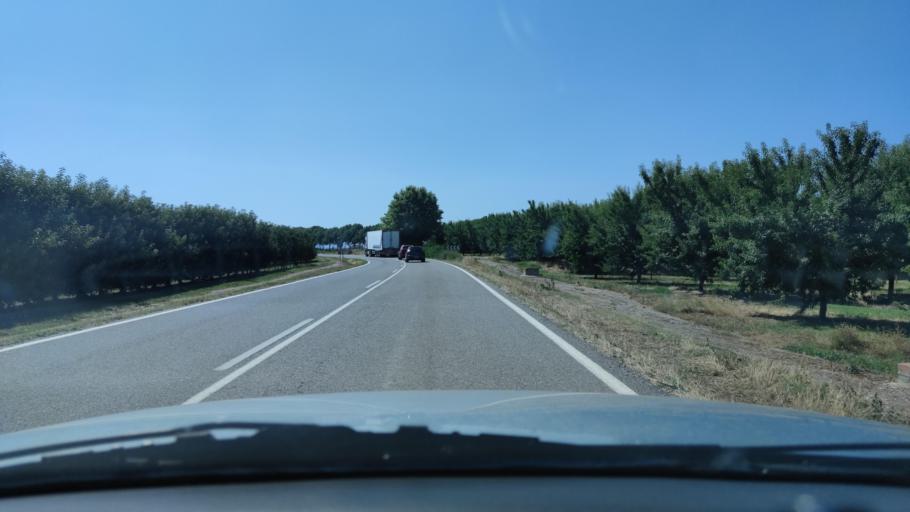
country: ES
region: Catalonia
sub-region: Provincia de Lleida
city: Ivars d'Urgell
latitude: 41.6947
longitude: 0.9863
